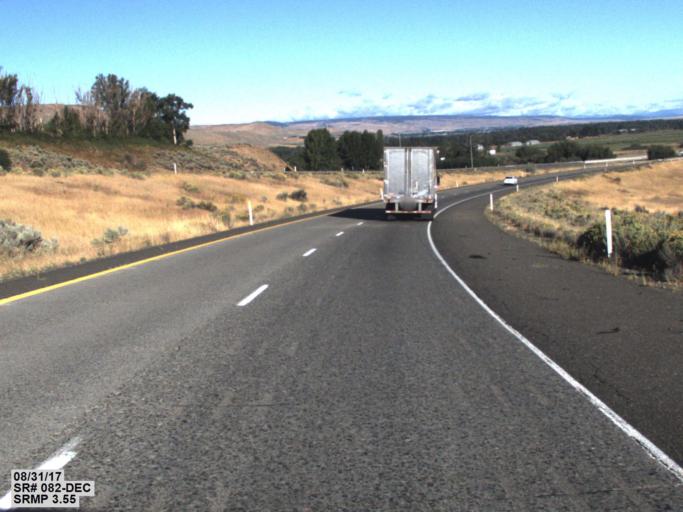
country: US
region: Washington
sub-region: Kittitas County
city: Ellensburg
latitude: 46.9231
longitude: -120.4940
